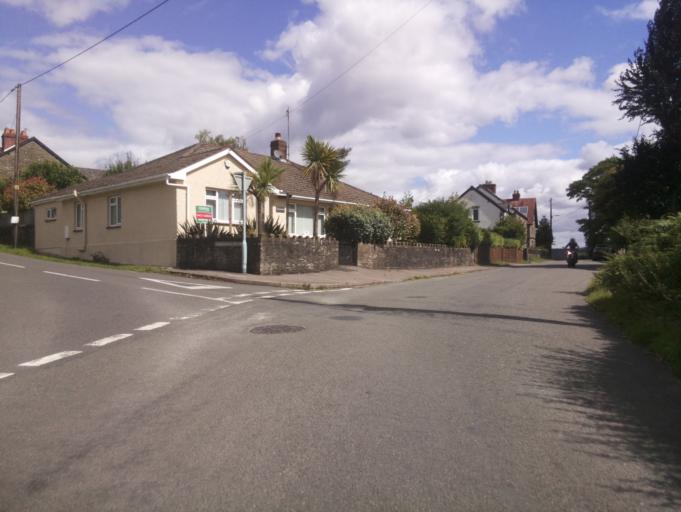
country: GB
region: England
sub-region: Gloucestershire
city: Bream
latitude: 51.7440
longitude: -2.5579
